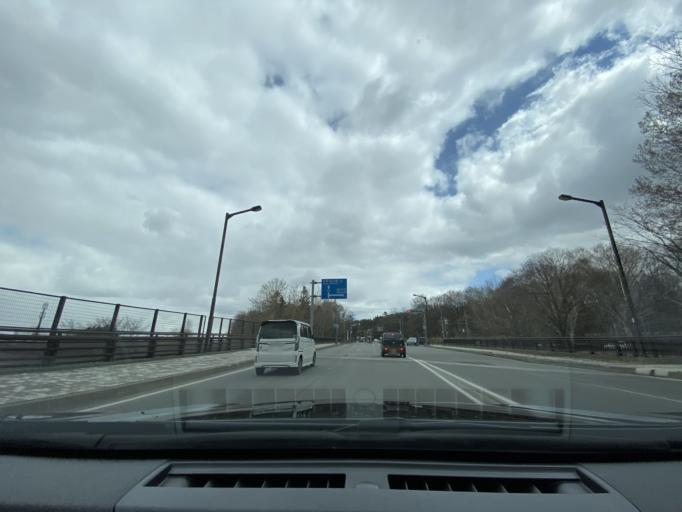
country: JP
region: Hokkaido
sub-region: Asahikawa-shi
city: Asahikawa
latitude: 43.7502
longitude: 142.3604
